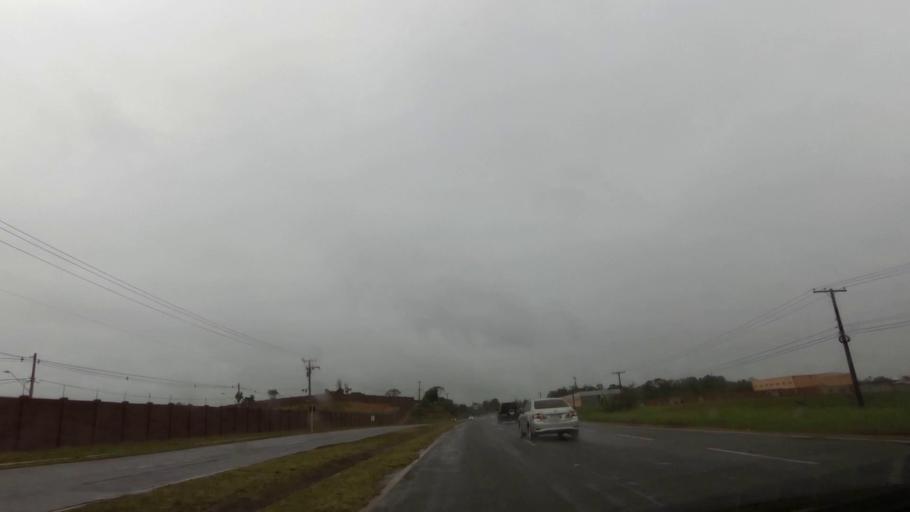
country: BR
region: Espirito Santo
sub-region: Vitoria
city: Vitoria
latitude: -20.4783
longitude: -40.3529
